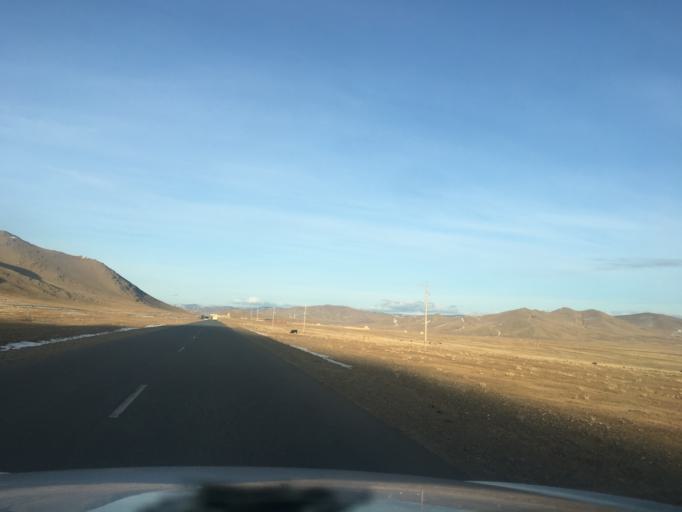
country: MN
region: Central Aimak
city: Mandal
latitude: 48.1131
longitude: 106.6396
